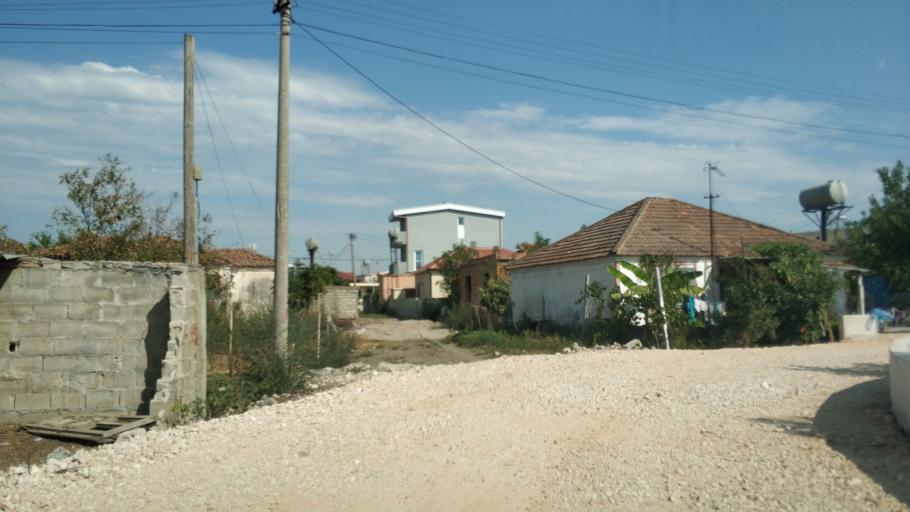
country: AL
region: Fier
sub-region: Rrethi i Lushnjes
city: Divjake
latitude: 40.9945
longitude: 19.5277
